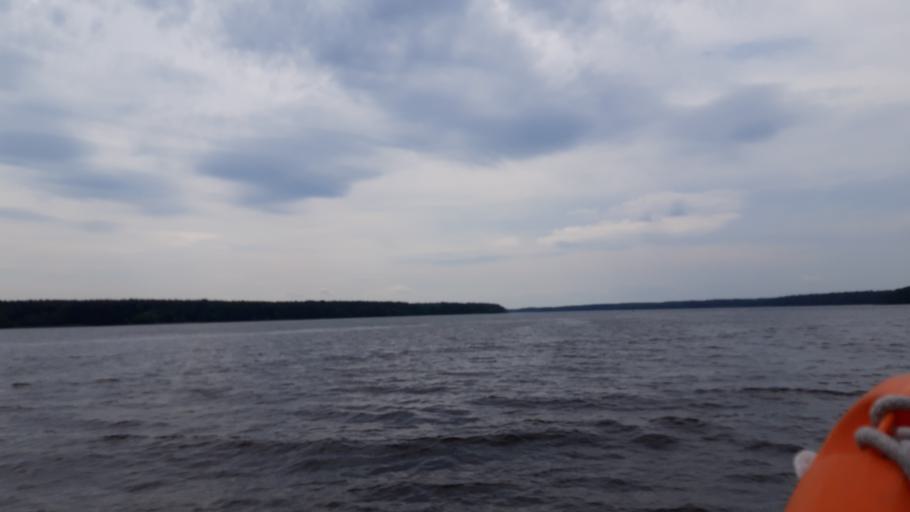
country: RU
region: Tverskaya
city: Konakovo
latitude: 56.7044
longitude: 36.7297
